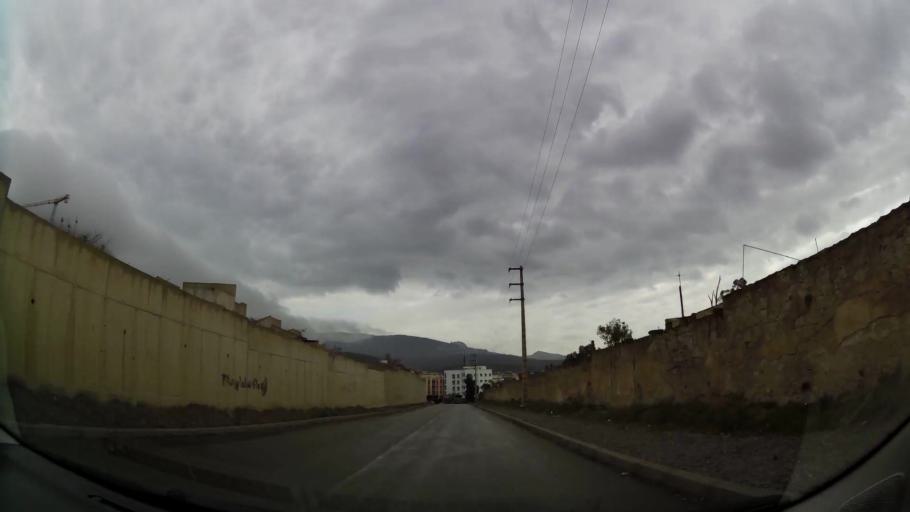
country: MA
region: Oriental
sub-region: Nador
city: Nador
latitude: 35.1506
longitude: -3.0075
